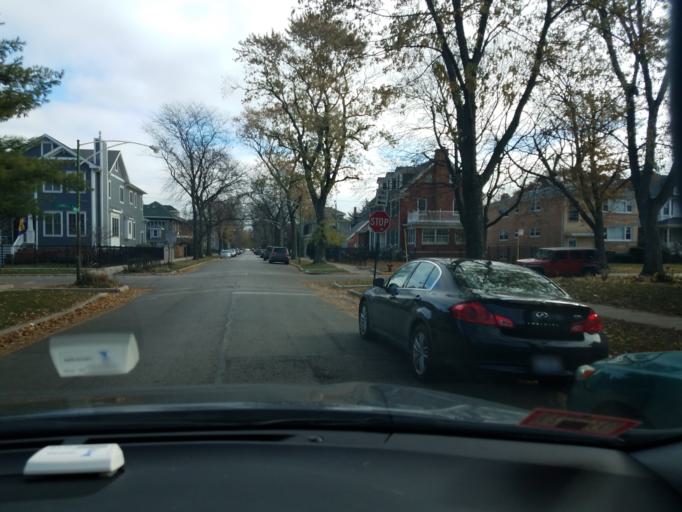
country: US
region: Illinois
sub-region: Cook County
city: Lincolnwood
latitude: 41.9517
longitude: -87.7371
